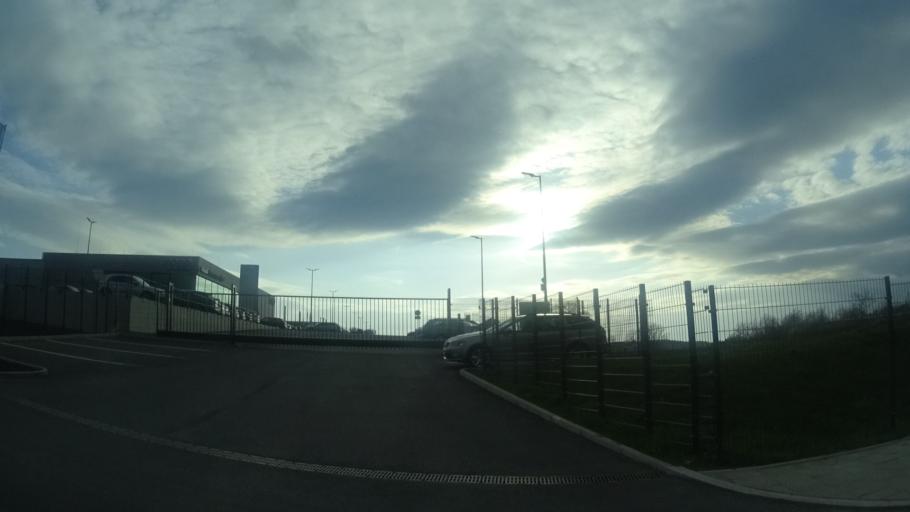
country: DE
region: Bavaria
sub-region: Upper Franconia
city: Koditz
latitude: 50.3107
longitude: 11.8738
